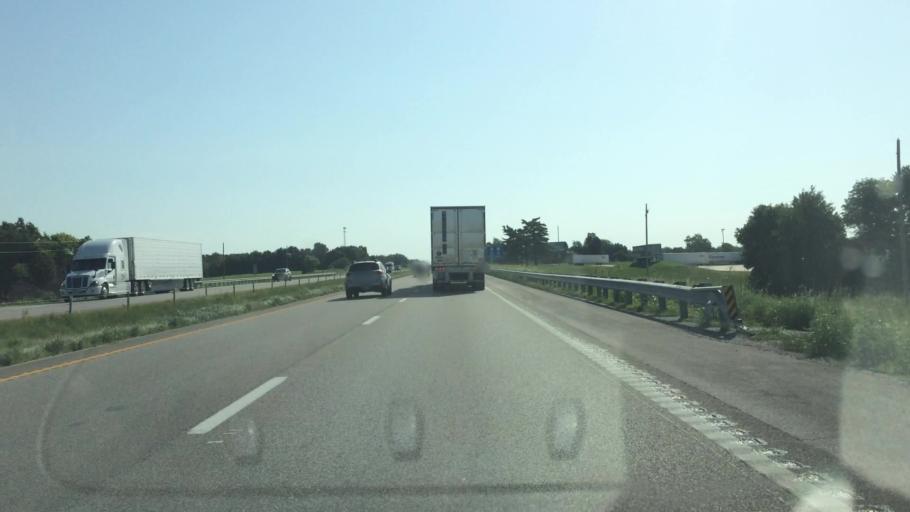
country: US
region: Missouri
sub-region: Greene County
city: Strafford
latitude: 37.2600
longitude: -93.1543
